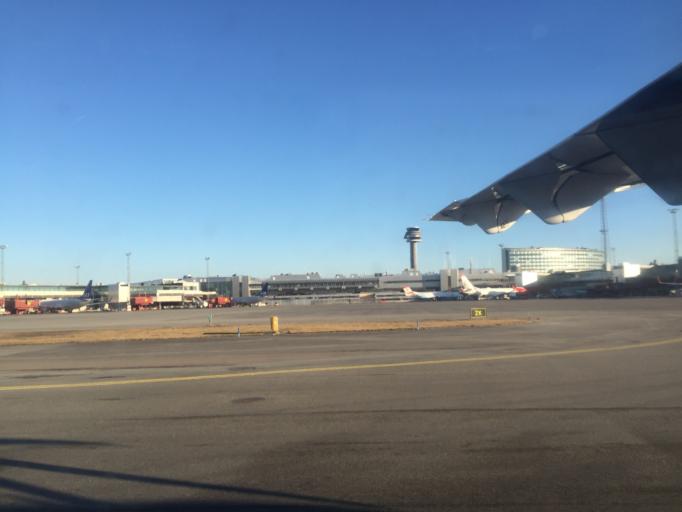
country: SE
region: Stockholm
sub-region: Sigtuna Kommun
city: Marsta
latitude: 59.6534
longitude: 17.9251
